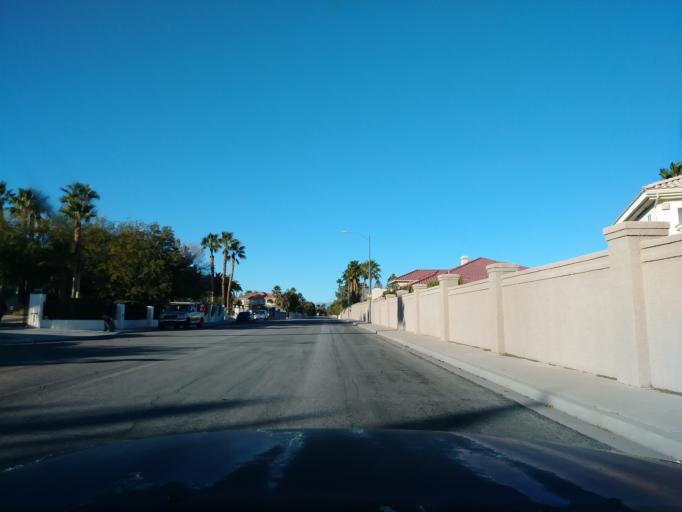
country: US
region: Nevada
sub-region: Clark County
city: Spring Valley
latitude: 36.1477
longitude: -115.2680
